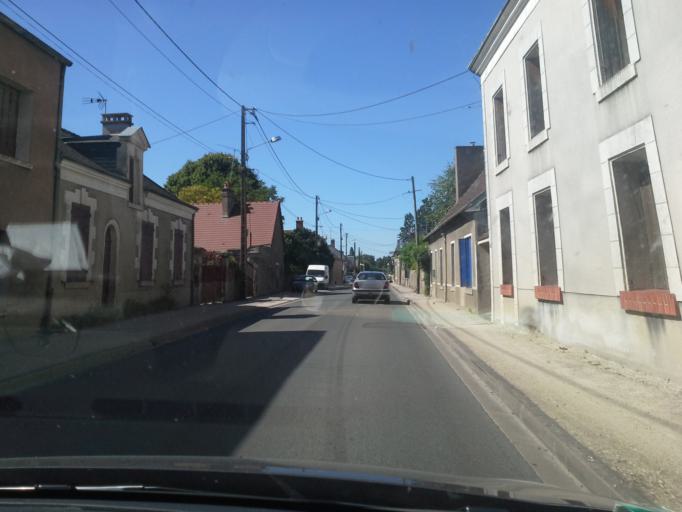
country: FR
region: Centre
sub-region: Departement du Loir-et-Cher
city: Cormeray
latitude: 47.4904
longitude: 1.4070
